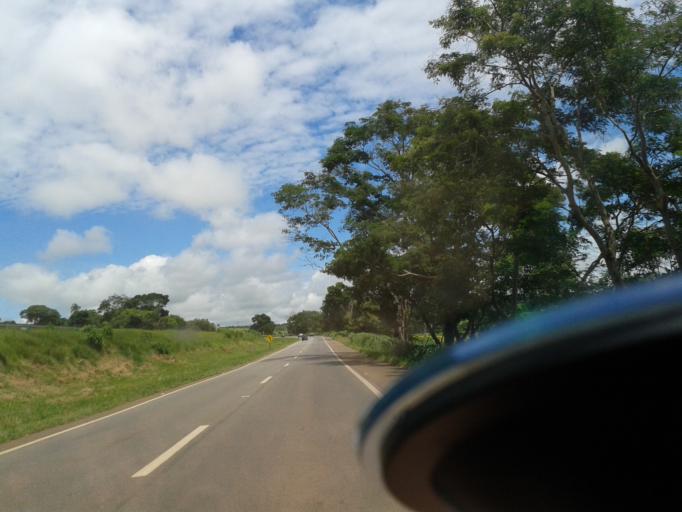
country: BR
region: Goias
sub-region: Inhumas
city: Inhumas
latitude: -16.2216
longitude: -49.5648
